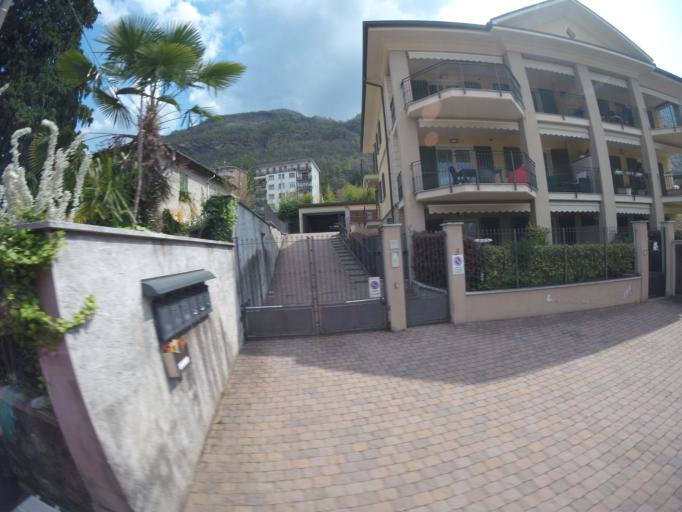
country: IT
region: Piedmont
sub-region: Provincia Verbano-Cusio-Ossola
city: Omegna
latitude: 45.8697
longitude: 8.4122
